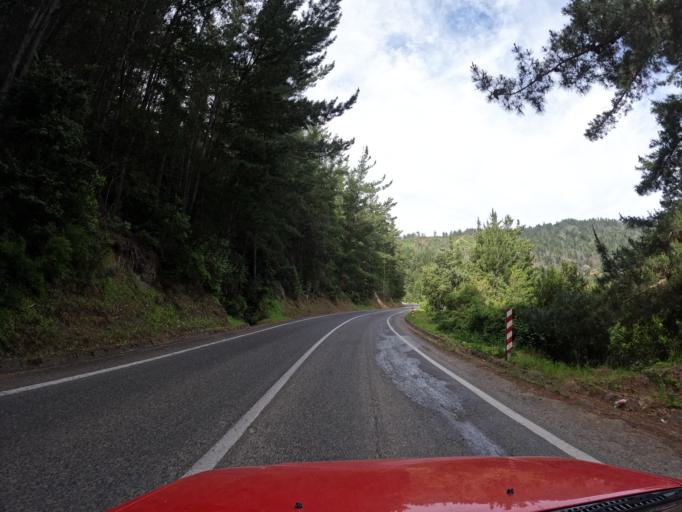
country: CL
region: Maule
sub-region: Provincia de Talca
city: Talca
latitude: -35.2974
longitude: -71.9674
